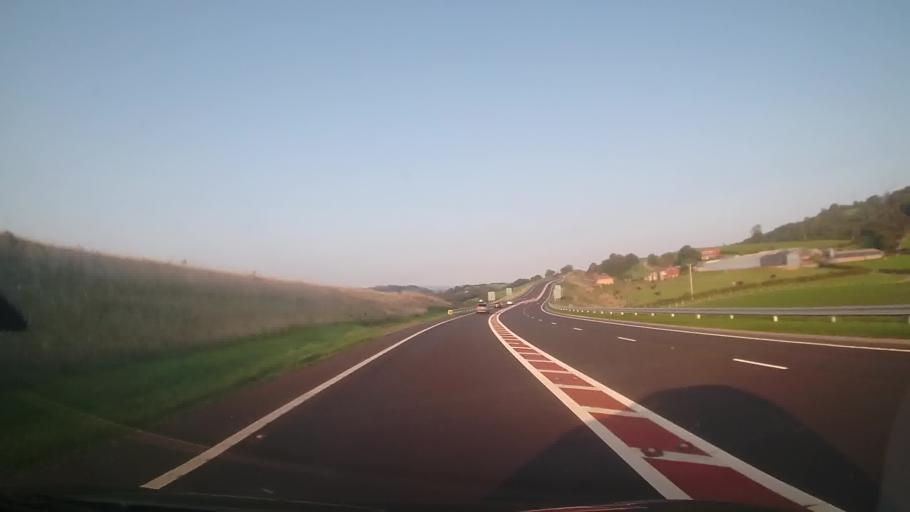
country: GB
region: Wales
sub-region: Sir Powys
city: Newtown
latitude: 52.5069
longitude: -3.3104
